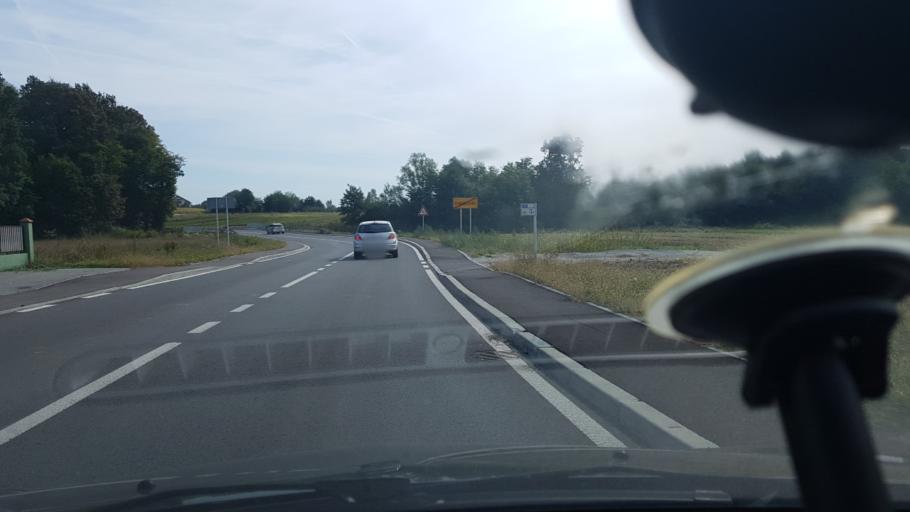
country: HR
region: Krapinsko-Zagorska
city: Marija Bistrica
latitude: 46.0512
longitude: 16.1210
